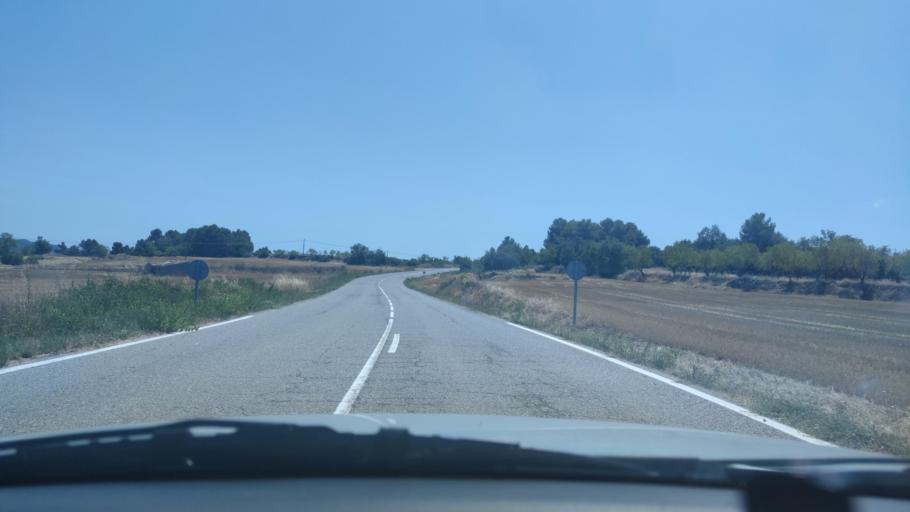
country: ES
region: Catalonia
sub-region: Provincia de Lleida
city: Vinaixa
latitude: 41.4219
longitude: 0.9510
